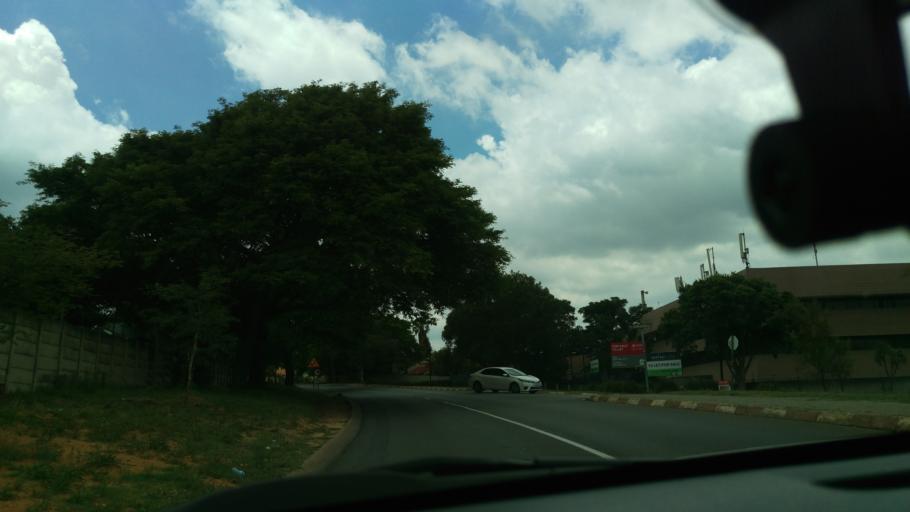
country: ZA
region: Gauteng
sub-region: City of Johannesburg Metropolitan Municipality
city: Midrand
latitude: -26.0478
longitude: 28.0526
